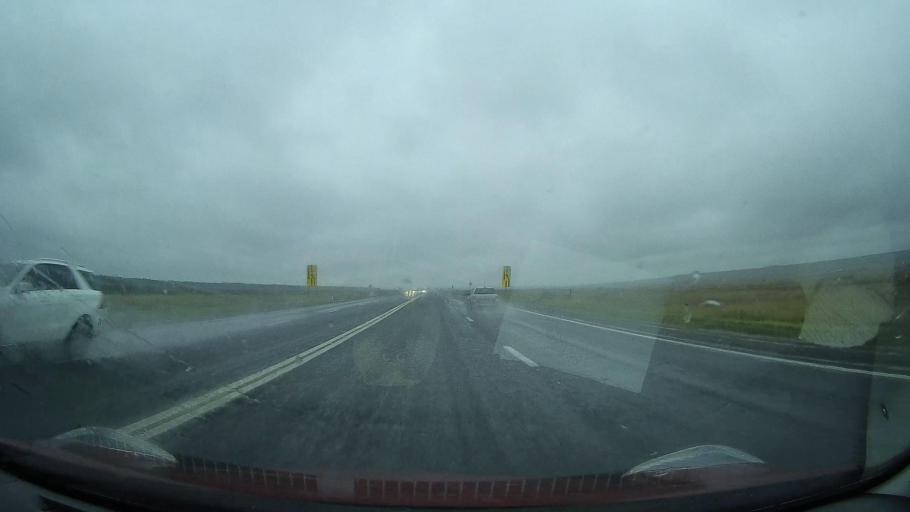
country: RU
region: Stavropol'skiy
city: Nevinnomyssk
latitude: 44.6244
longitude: 42.0653
